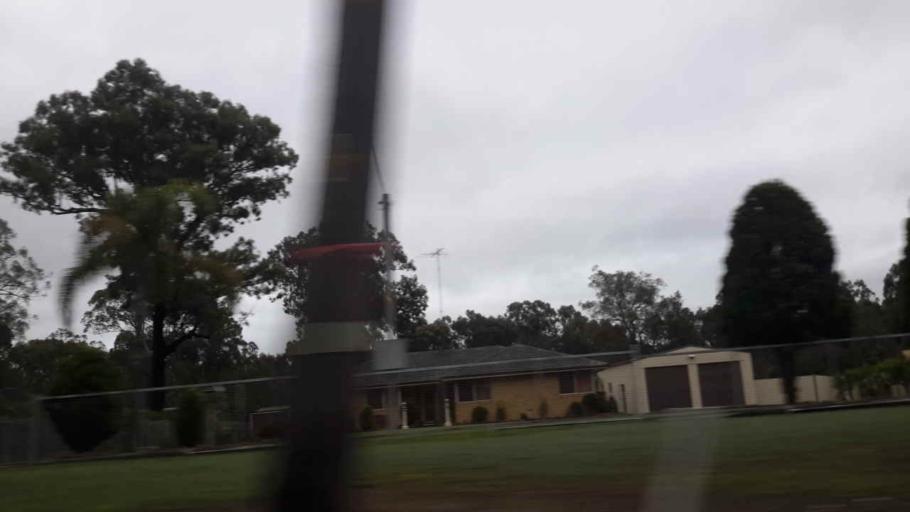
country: AU
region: New South Wales
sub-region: Hawkesbury
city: South Windsor
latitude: -33.6494
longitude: 150.7774
